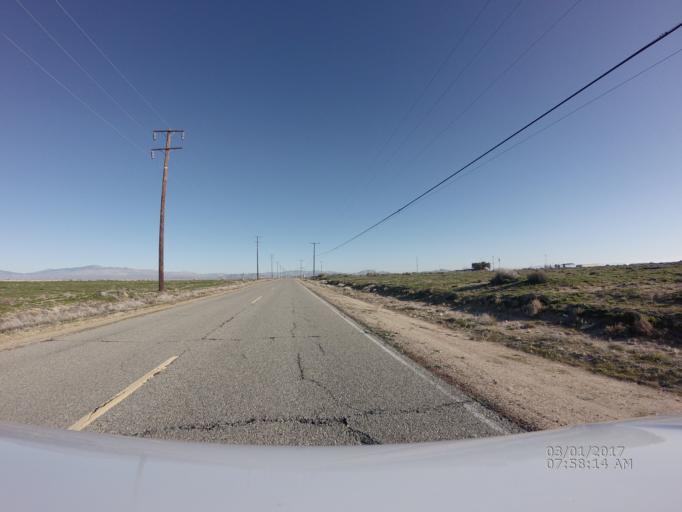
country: US
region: California
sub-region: Kern County
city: Rosamond
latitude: 34.7713
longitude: -118.2548
